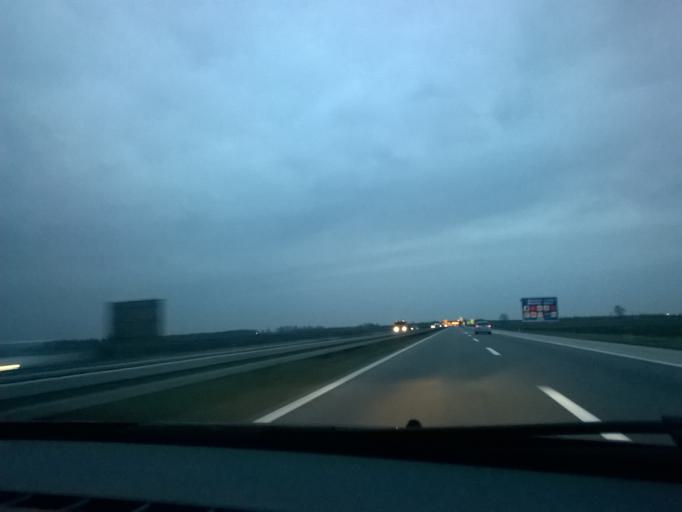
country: RS
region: Autonomna Pokrajina Vojvodina
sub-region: Sremski Okrug
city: Stara Pazova
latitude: 45.0176
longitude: 20.1951
